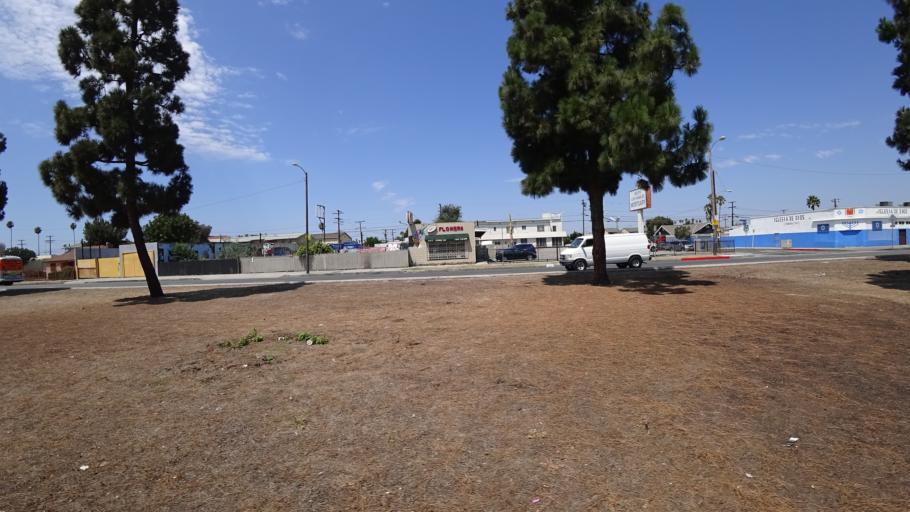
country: US
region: California
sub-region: Los Angeles County
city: Westmont
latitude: 33.9506
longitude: -118.2916
